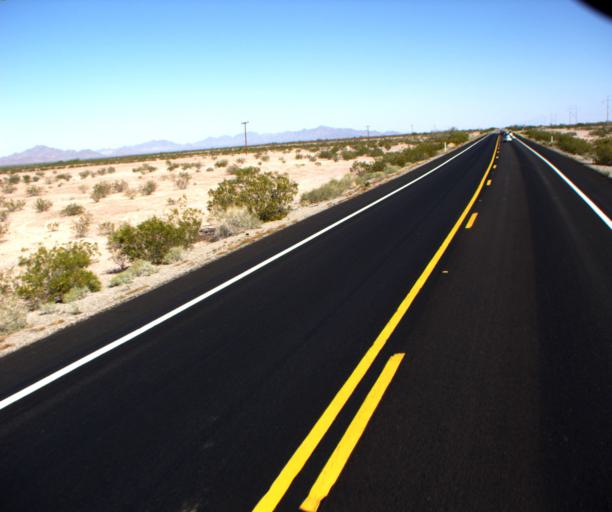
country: US
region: Arizona
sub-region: La Paz County
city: Quartzsite
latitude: 33.3088
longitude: -114.2169
